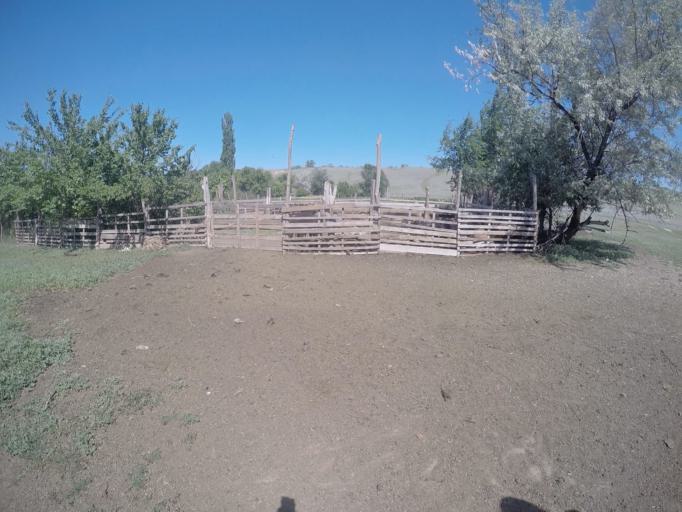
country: RU
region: Saratov
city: Krasnoarmeysk
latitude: 51.1535
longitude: 45.9304
